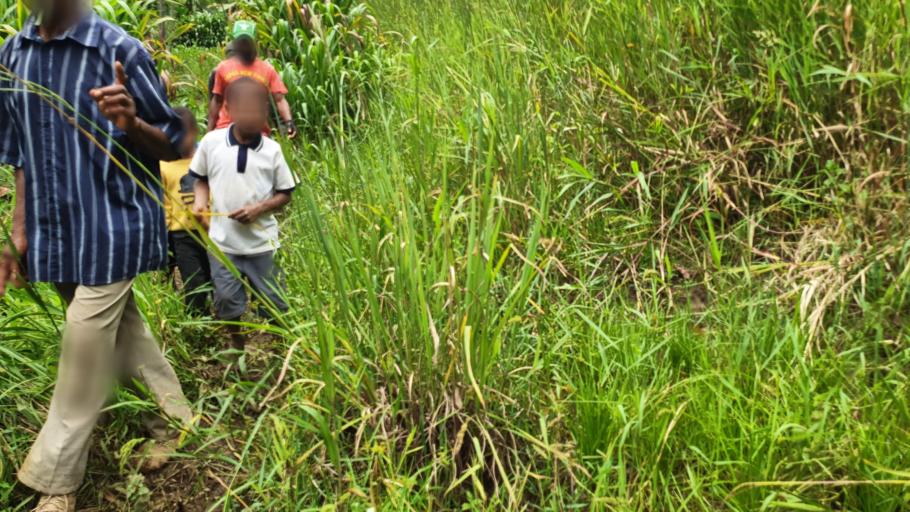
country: PG
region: Jiwaka
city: Minj
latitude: -5.9130
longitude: 144.8308
